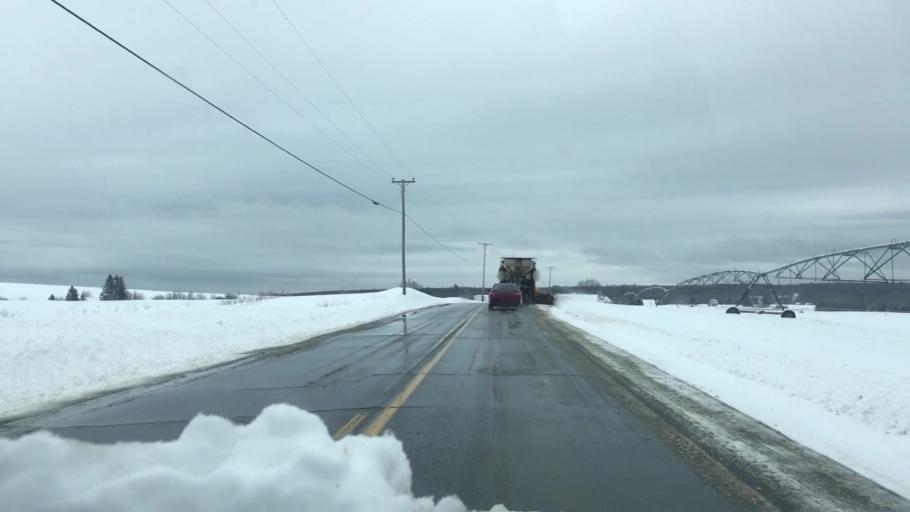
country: US
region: Maine
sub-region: Penobscot County
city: Garland
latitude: 44.9783
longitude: -69.1024
